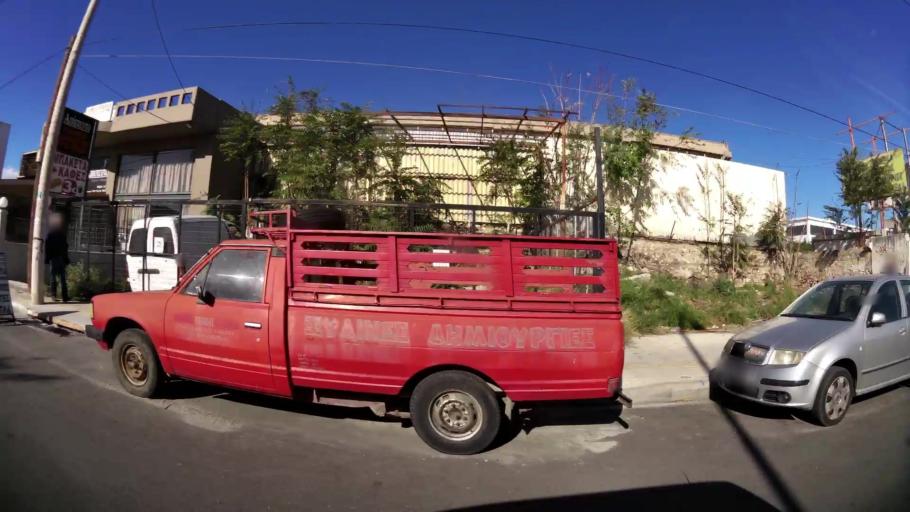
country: GR
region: Attica
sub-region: Nomarchia Athinas
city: Aigaleo
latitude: 37.9818
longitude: 23.6716
